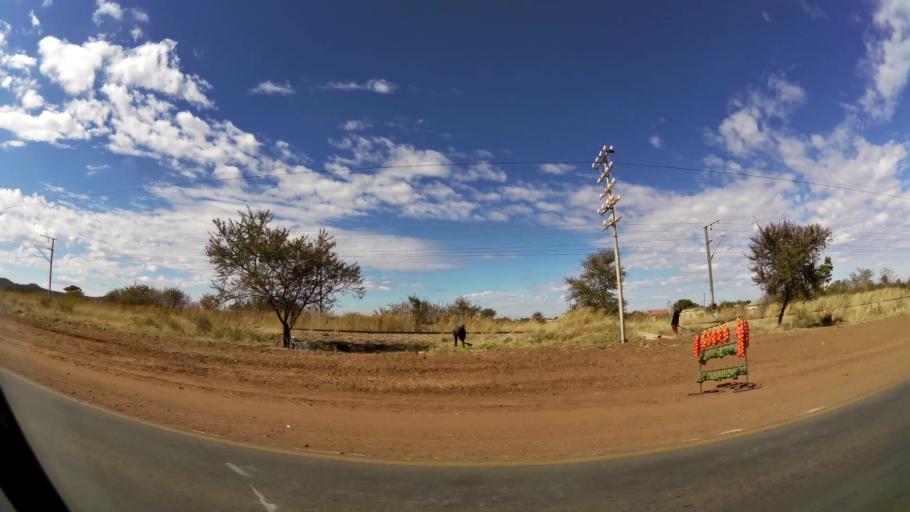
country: ZA
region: Limpopo
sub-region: Waterberg District Municipality
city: Bela-Bela
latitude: -24.8696
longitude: 28.3218
